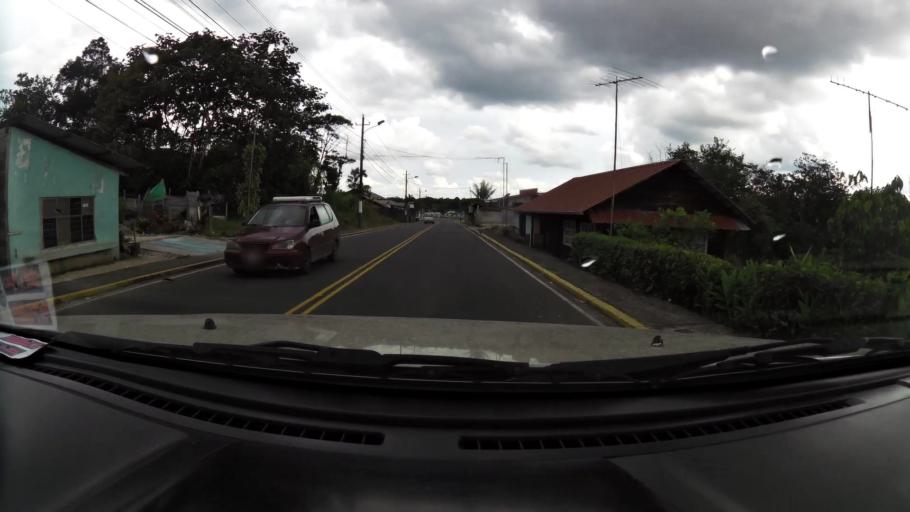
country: EC
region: Pastaza
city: Puyo
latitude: -1.4627
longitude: -78.1119
